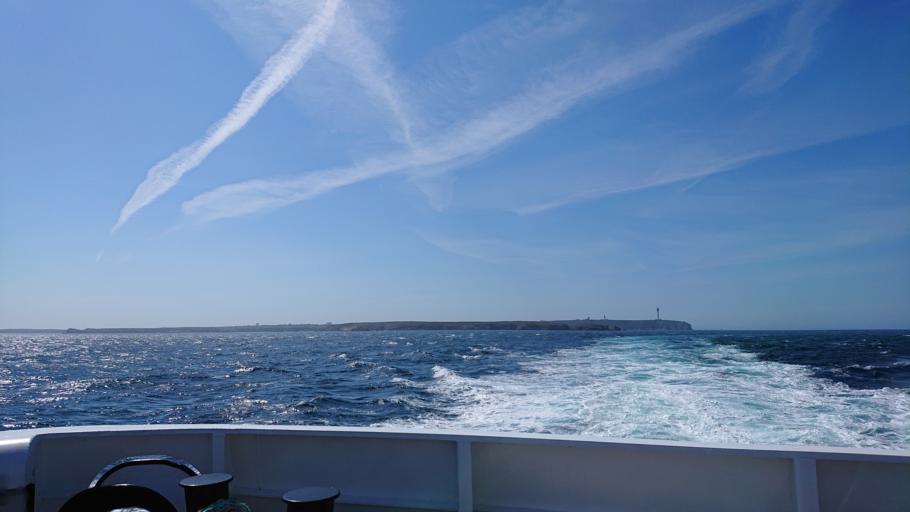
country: FR
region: Brittany
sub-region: Departement du Finistere
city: Porspoder
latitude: 48.4546
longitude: -5.0135
